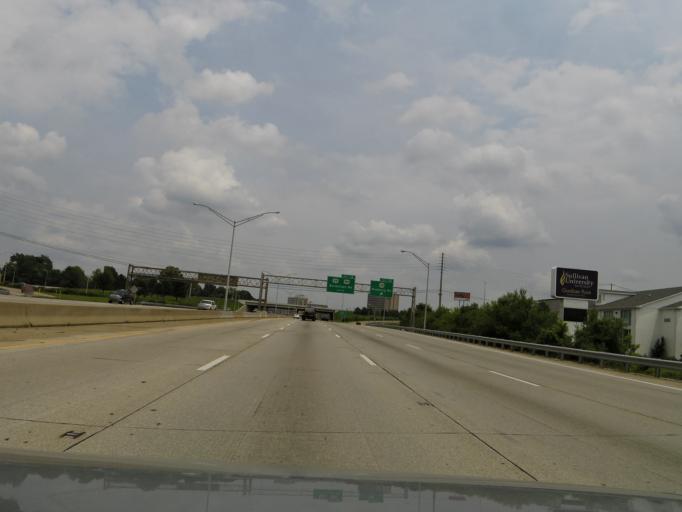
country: US
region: Kentucky
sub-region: Jefferson County
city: West Buechel
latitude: 38.2009
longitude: -85.6936
